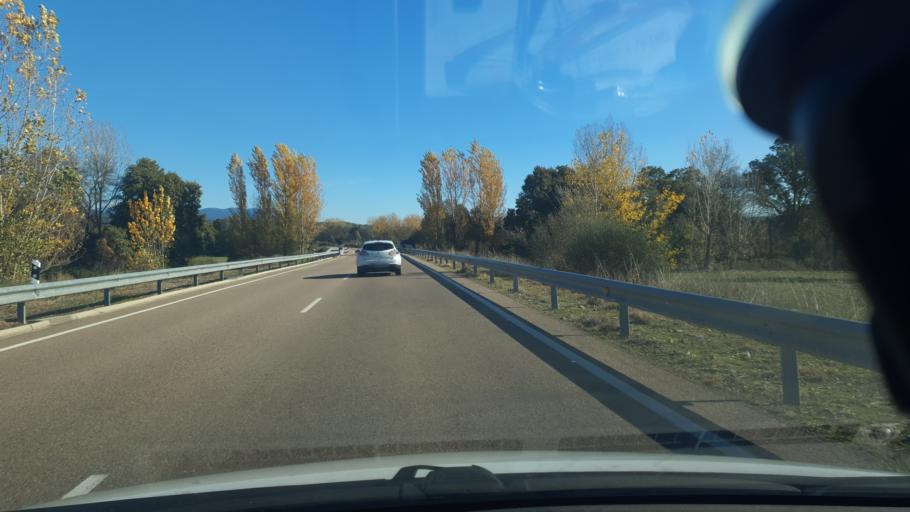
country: ES
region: Castille and Leon
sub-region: Provincia de Avila
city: Candeleda
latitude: 40.1390
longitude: -5.2109
